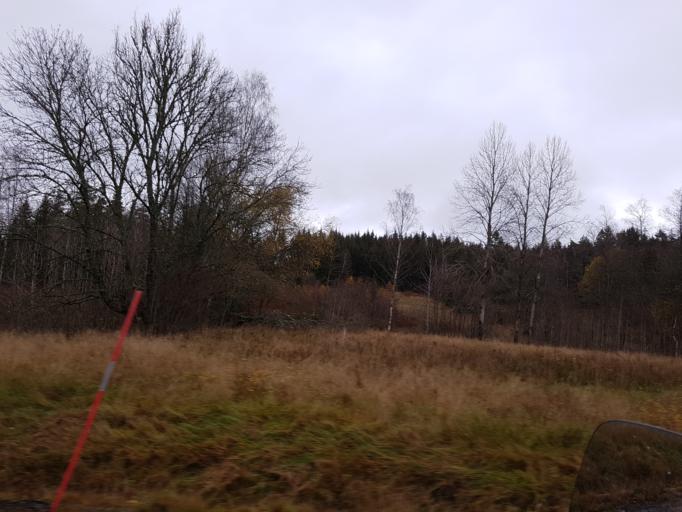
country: SE
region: Vaestra Goetaland
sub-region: Orust
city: Henan
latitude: 58.2290
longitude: 11.7322
